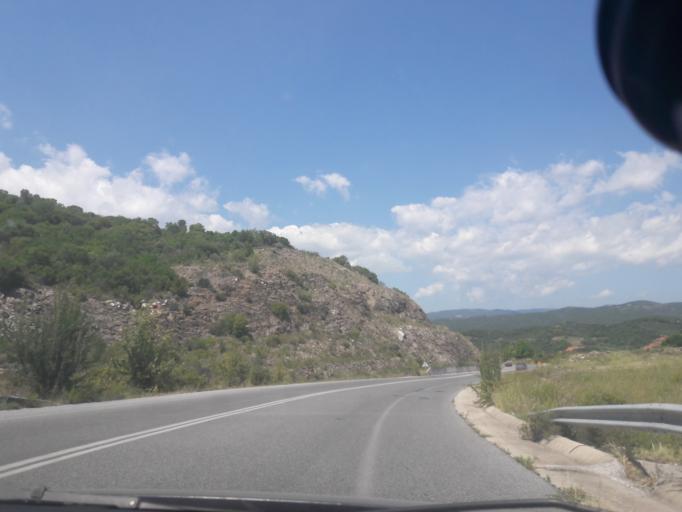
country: GR
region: Central Macedonia
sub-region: Nomos Chalkidikis
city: Ormylia
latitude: 40.3688
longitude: 23.6074
